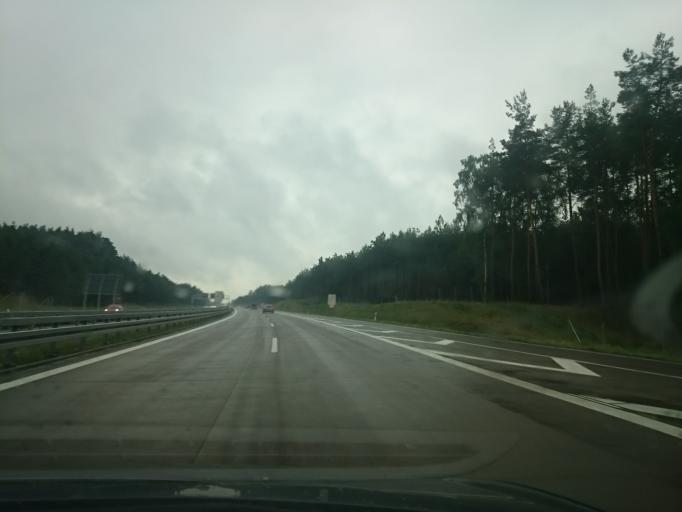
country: DE
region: Brandenburg
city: Kremmen
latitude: 52.7069
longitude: 13.0116
